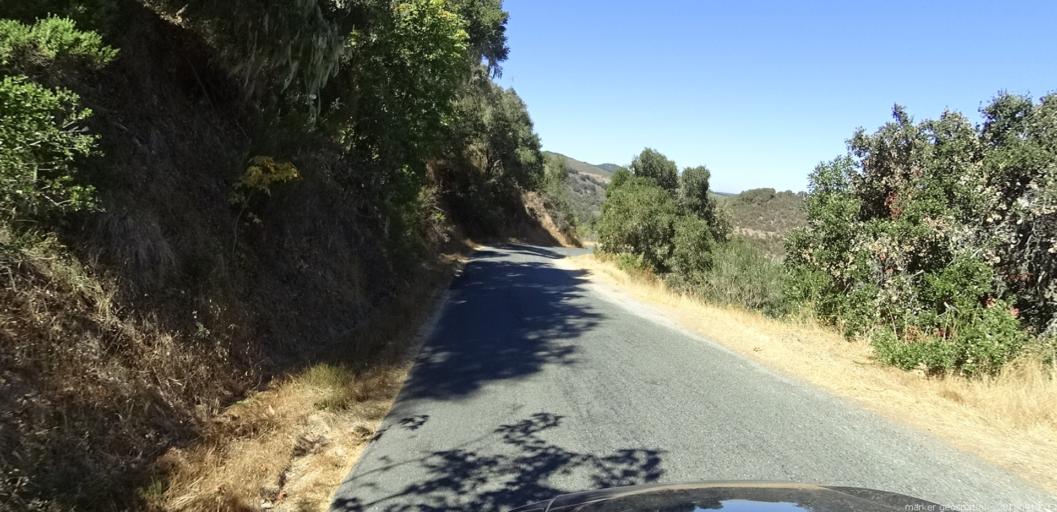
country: US
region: California
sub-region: Monterey County
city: Carmel Valley Village
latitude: 36.4860
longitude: -121.8065
